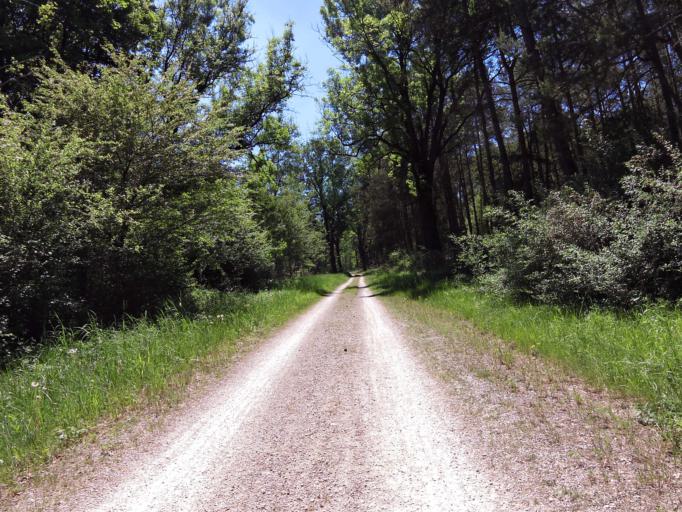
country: DE
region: Bavaria
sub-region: Upper Bavaria
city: Hallbergmoos
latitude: 48.3344
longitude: 11.7132
